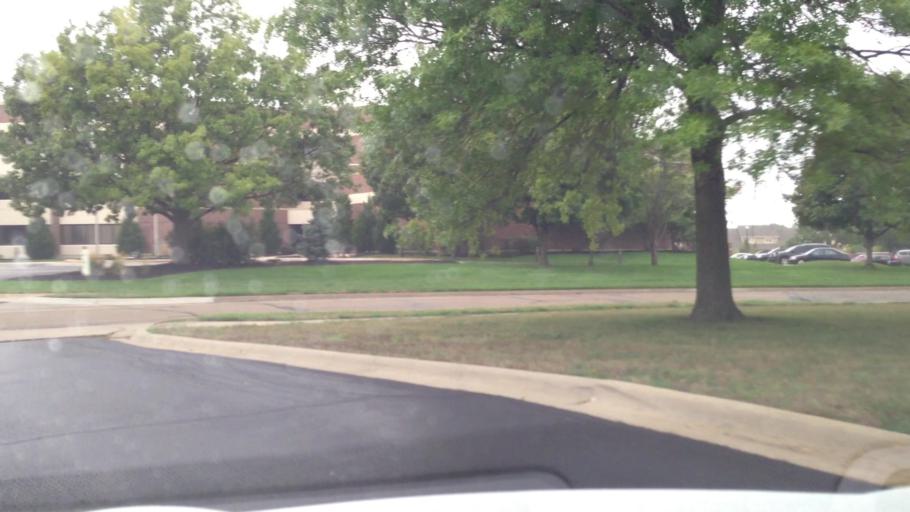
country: US
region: Kansas
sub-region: Douglas County
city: Lawrence
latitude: 38.9574
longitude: -95.3103
